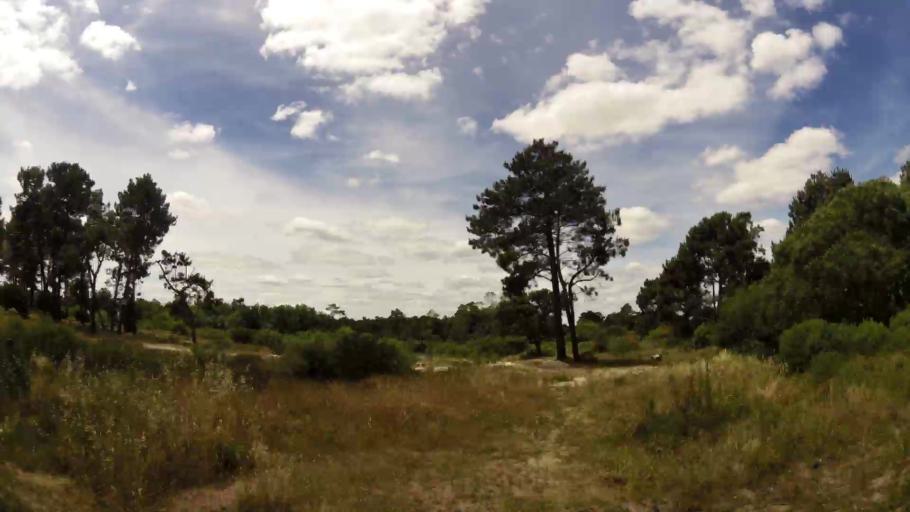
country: UY
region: Canelones
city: Empalme Olmos
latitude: -34.7899
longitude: -55.8893
